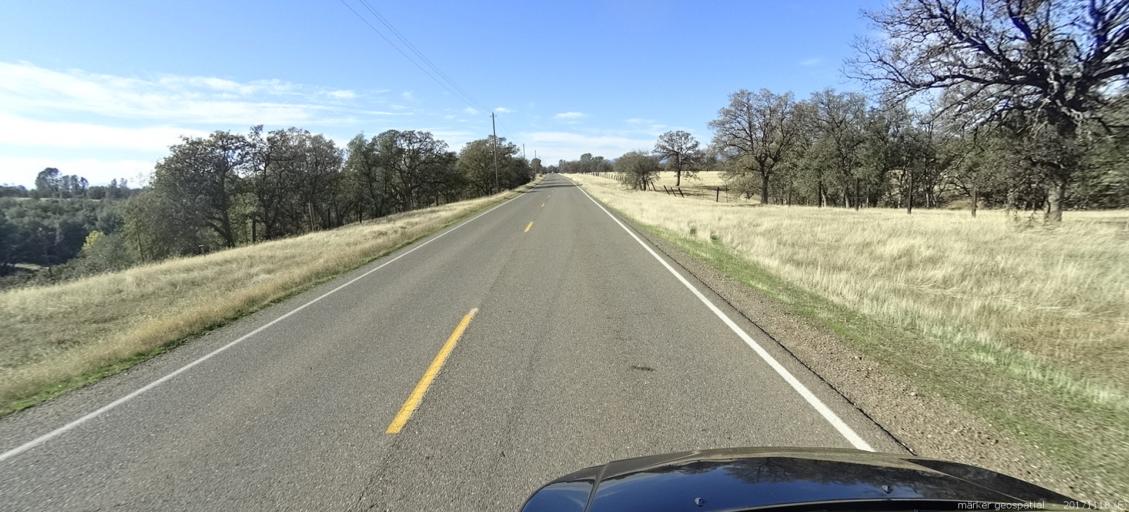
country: US
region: California
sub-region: Shasta County
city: Anderson
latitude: 40.4412
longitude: -122.3529
